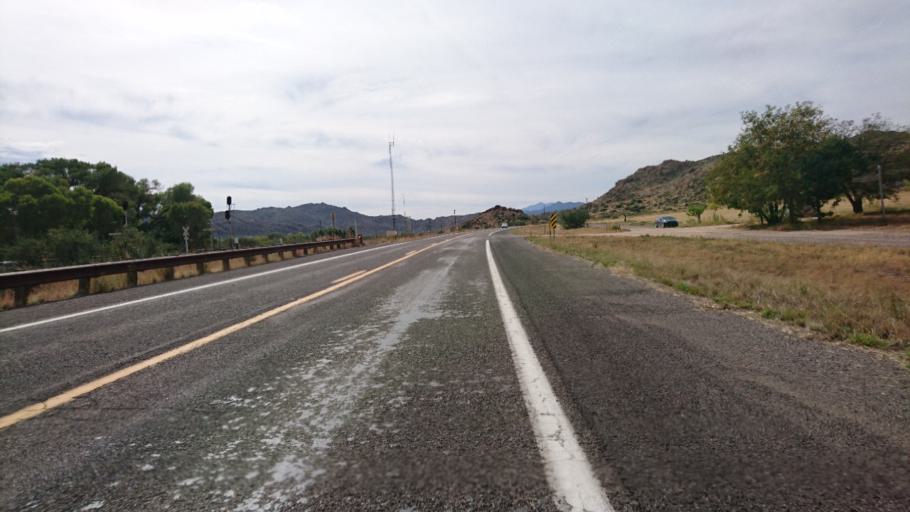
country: US
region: Arizona
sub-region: Mohave County
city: Peach Springs
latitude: 35.3873
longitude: -113.6590
